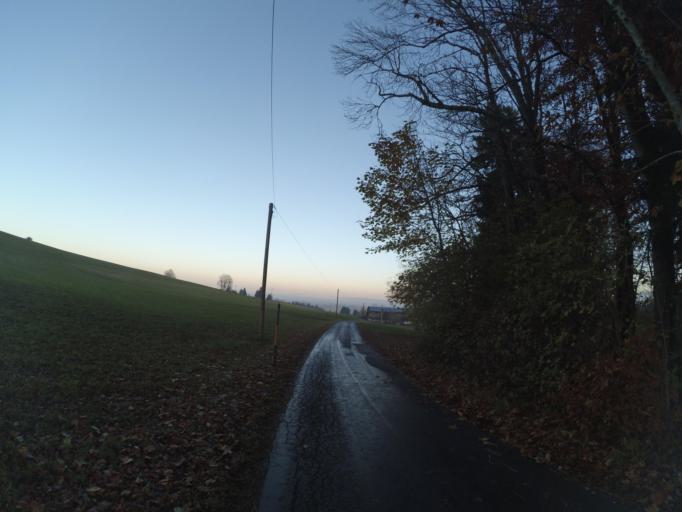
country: DE
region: Bavaria
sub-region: Upper Bavaria
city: Bernbeuren
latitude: 47.7396
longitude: 10.7519
